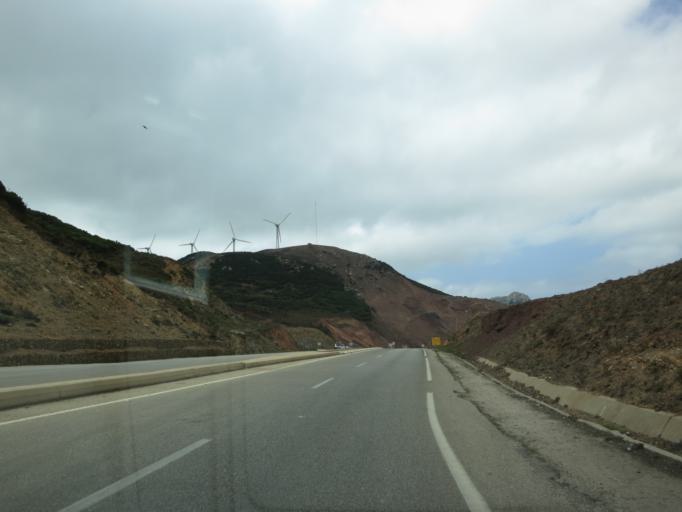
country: ES
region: Ceuta
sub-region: Ceuta
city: Ceuta
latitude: 35.8539
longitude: -5.4338
